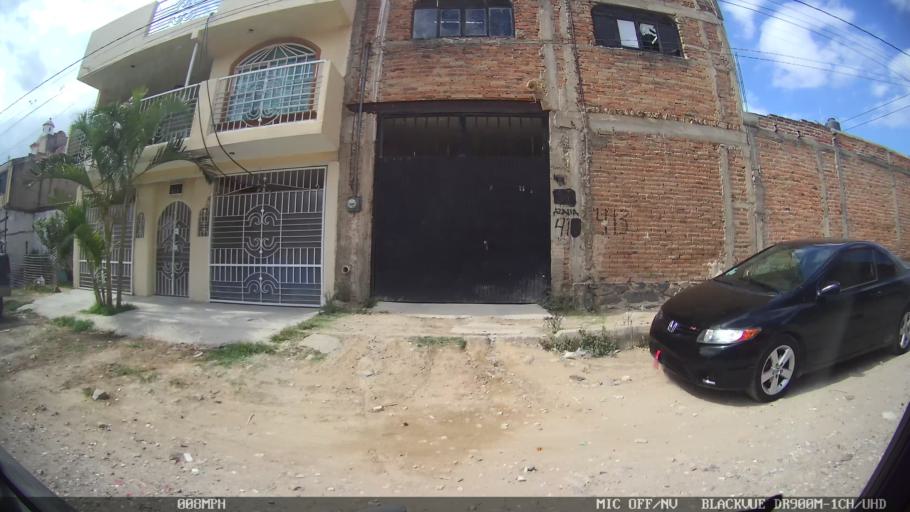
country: MX
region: Jalisco
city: Tonala
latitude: 20.6720
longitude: -103.2502
